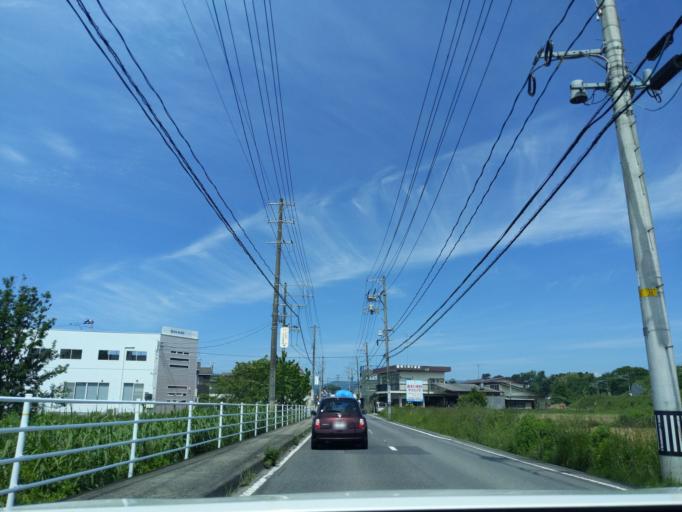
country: JP
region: Fukushima
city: Koriyama
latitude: 37.4139
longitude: 140.3759
